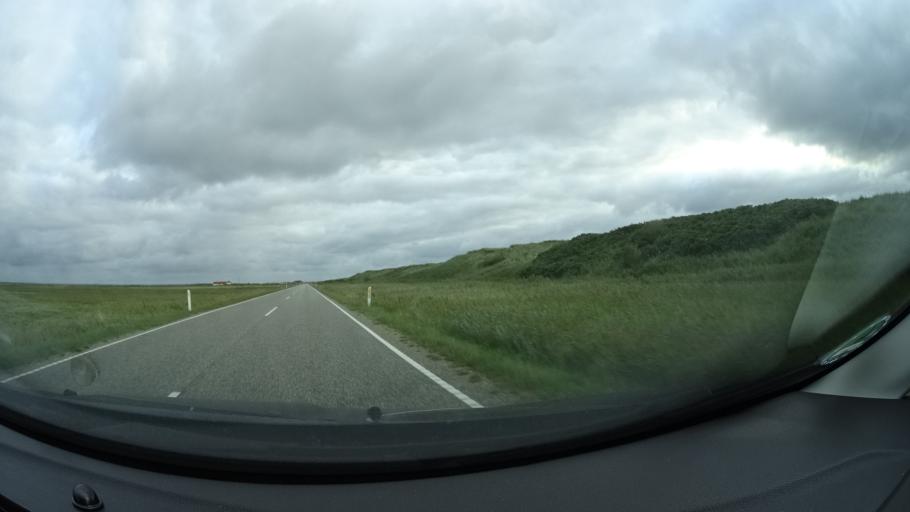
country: DK
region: Central Jutland
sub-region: Lemvig Kommune
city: Harboore
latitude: 56.3923
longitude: 8.1214
